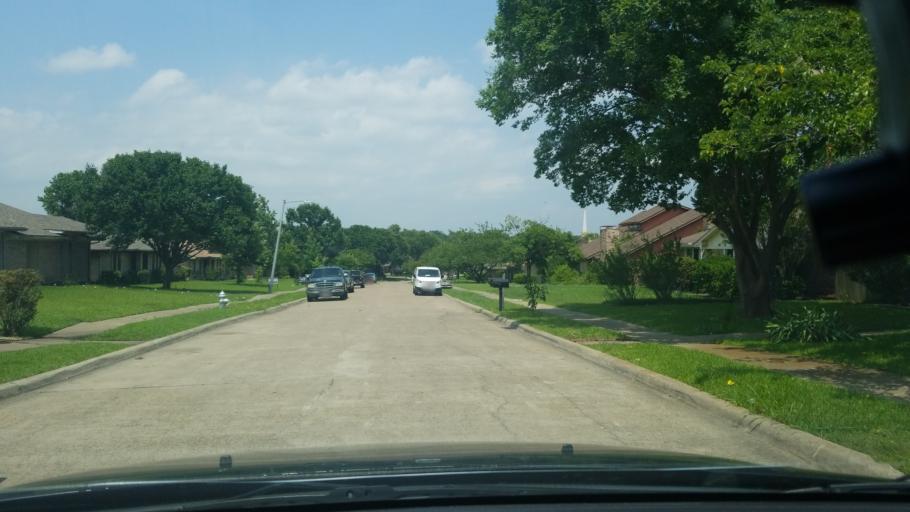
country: US
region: Texas
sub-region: Dallas County
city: Mesquite
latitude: 32.8064
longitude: -96.6427
